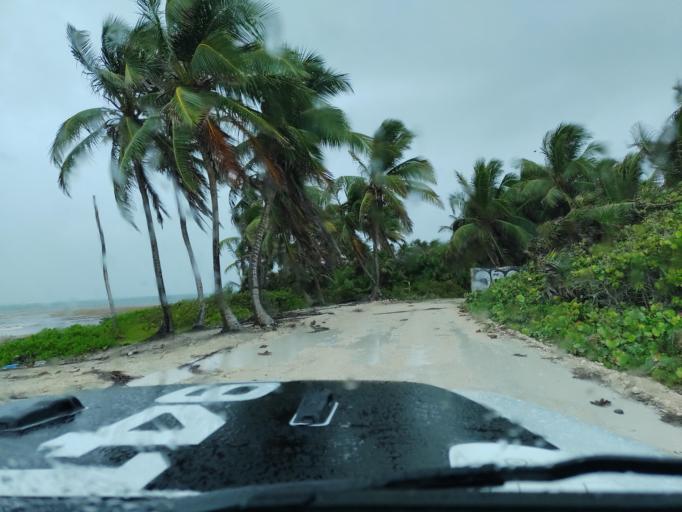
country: MX
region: Quintana Roo
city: Tulum
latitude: 19.9772
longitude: -87.4680
